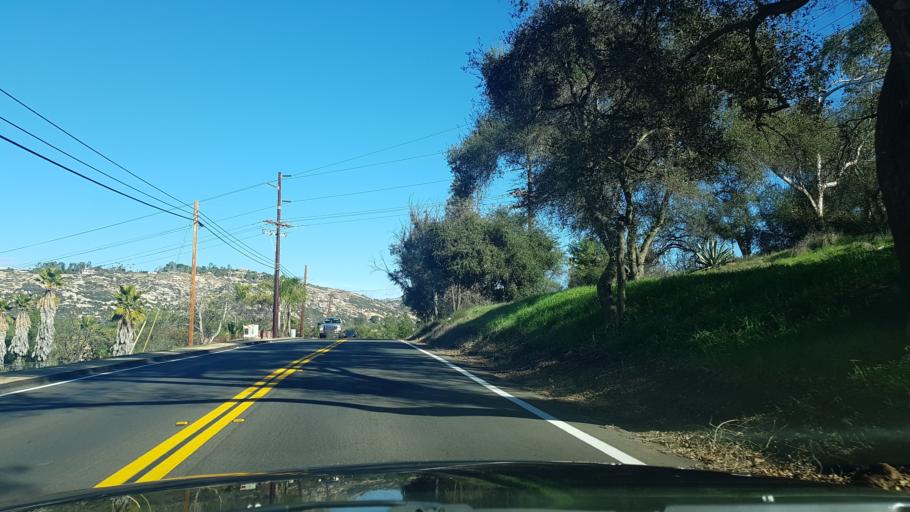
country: US
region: California
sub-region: San Diego County
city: Valley Center
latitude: 33.2071
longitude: -117.0292
